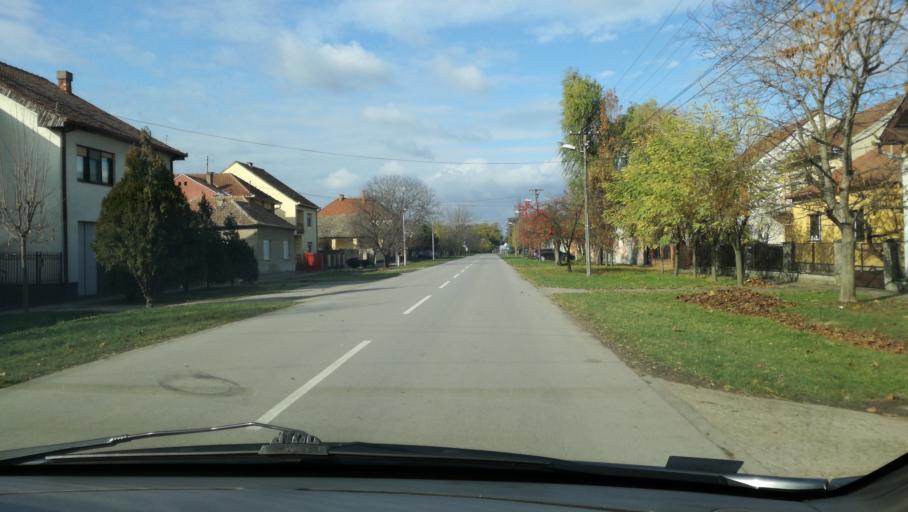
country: RS
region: Autonomna Pokrajina Vojvodina
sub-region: Severnobanatski Okrug
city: Kikinda
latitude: 45.8363
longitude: 20.4560
